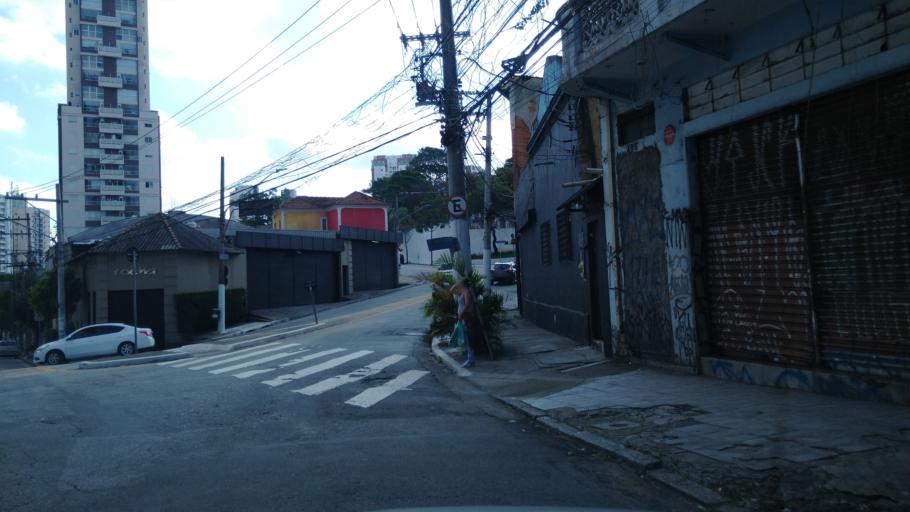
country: BR
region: Sao Paulo
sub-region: Sao Paulo
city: Sao Paulo
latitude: -23.4962
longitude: -46.6369
